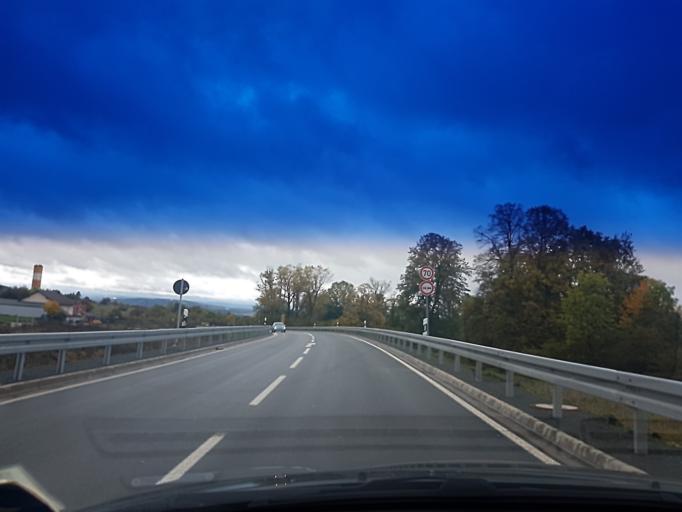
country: DE
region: Bavaria
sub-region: Upper Franconia
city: Bindlach
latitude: 49.9955
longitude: 11.6230
